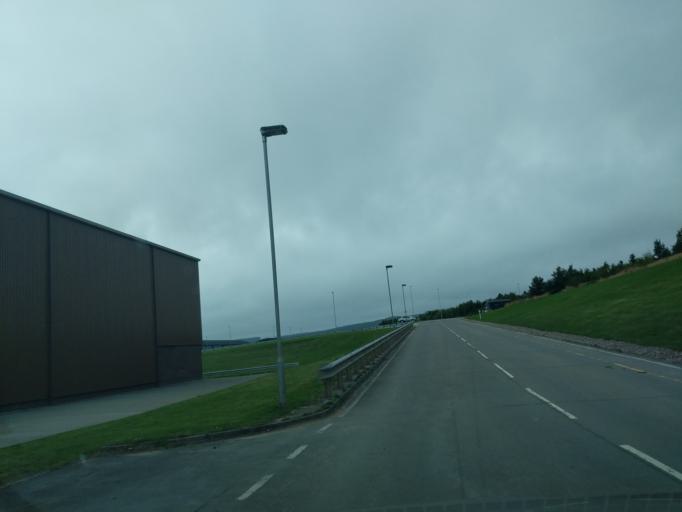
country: GB
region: Scotland
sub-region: Moray
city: Rothes
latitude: 57.4904
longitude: -3.2116
